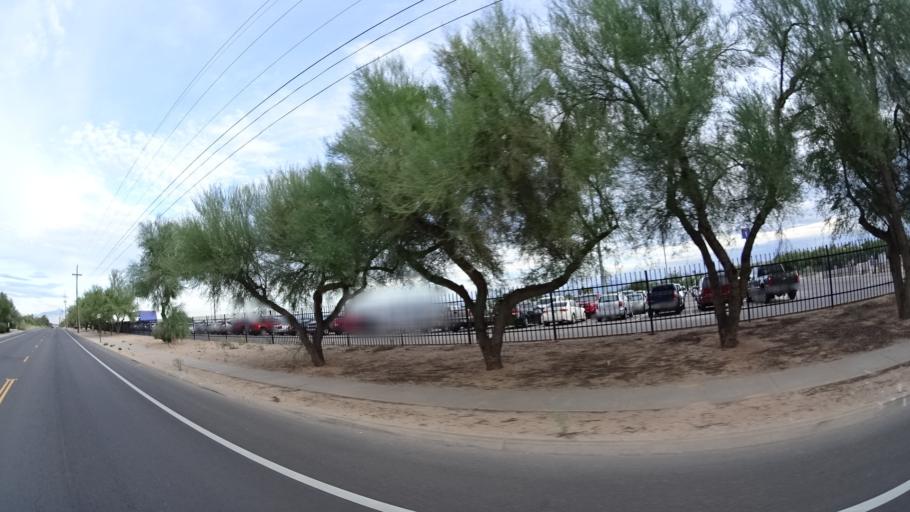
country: US
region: Arizona
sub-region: Pima County
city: Summit
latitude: 32.1232
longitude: -110.9335
